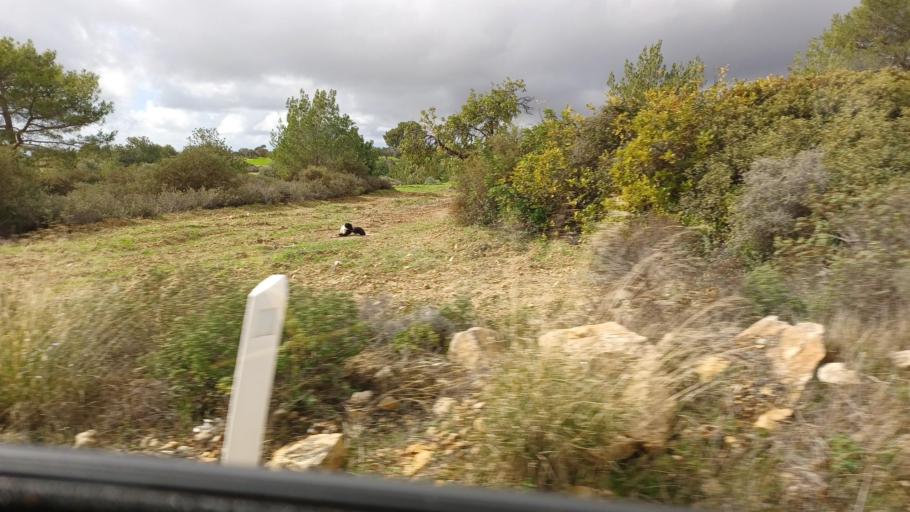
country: CY
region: Limassol
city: Sotira
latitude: 34.7261
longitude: 32.8656
